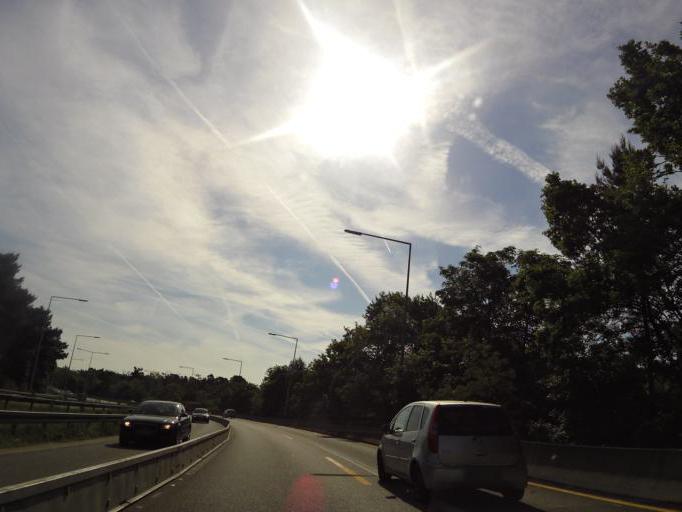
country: DE
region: Hesse
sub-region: Regierungsbezirk Darmstadt
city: Darmstadt
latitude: 49.8667
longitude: 8.6123
